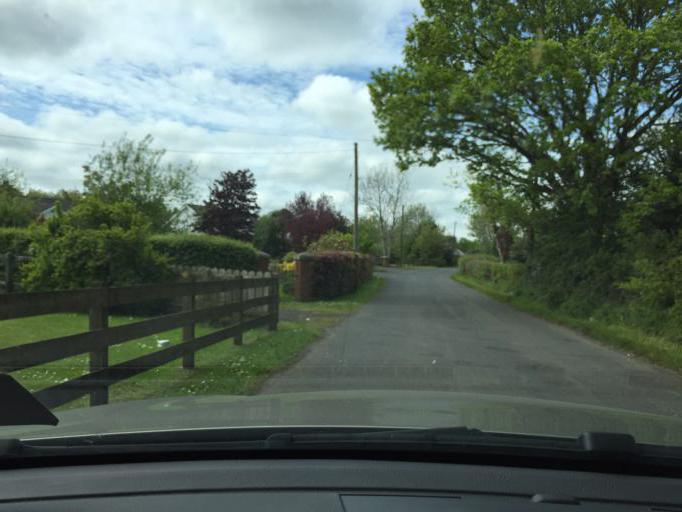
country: GB
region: Northern Ireland
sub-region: Craigavon District
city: Craigavon
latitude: 54.4571
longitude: -6.4086
